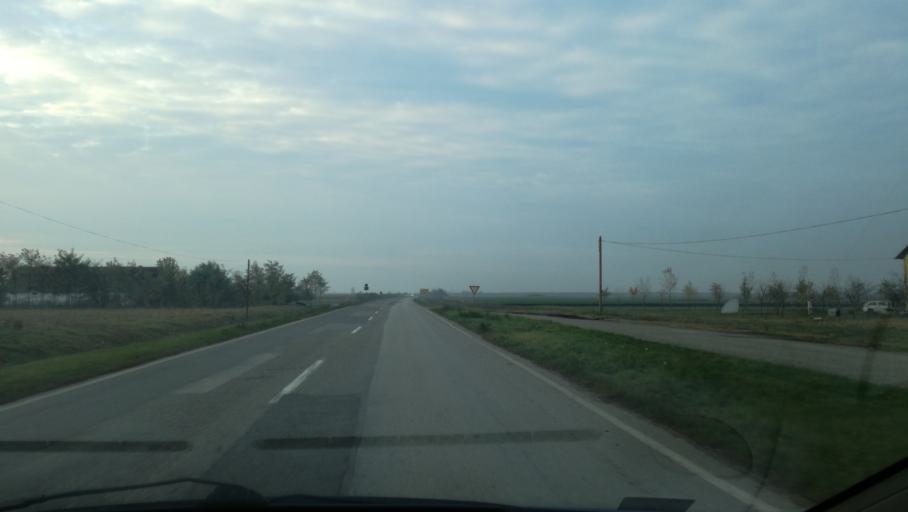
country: RS
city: Basaid
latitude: 45.6766
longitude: 20.4226
